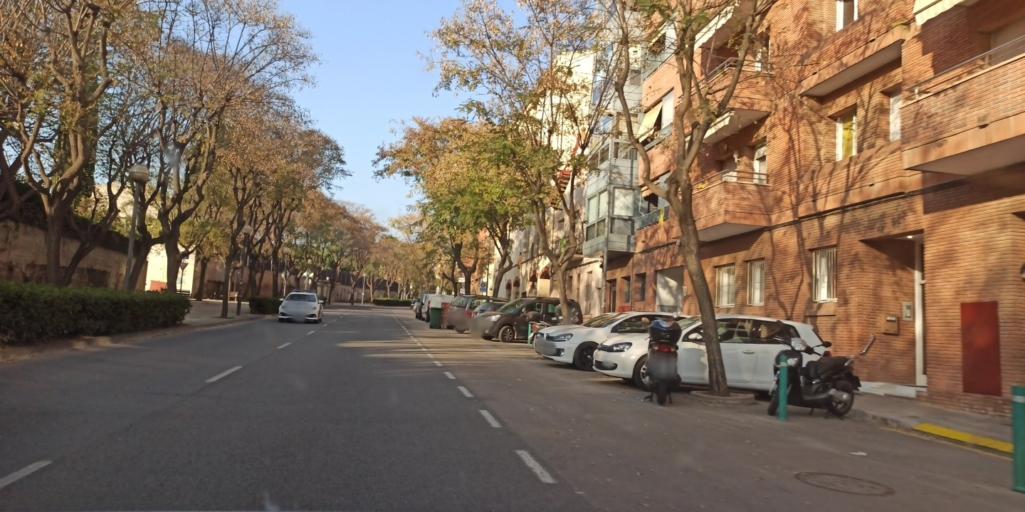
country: ES
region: Catalonia
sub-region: Provincia de Barcelona
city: Sant Just Desvern
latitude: 41.3843
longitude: 2.0723
